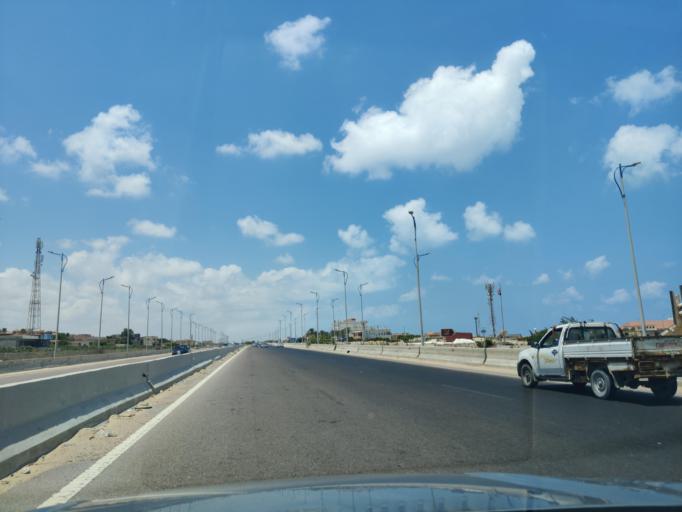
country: EG
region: Alexandria
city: Alexandria
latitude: 30.9684
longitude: 29.5581
